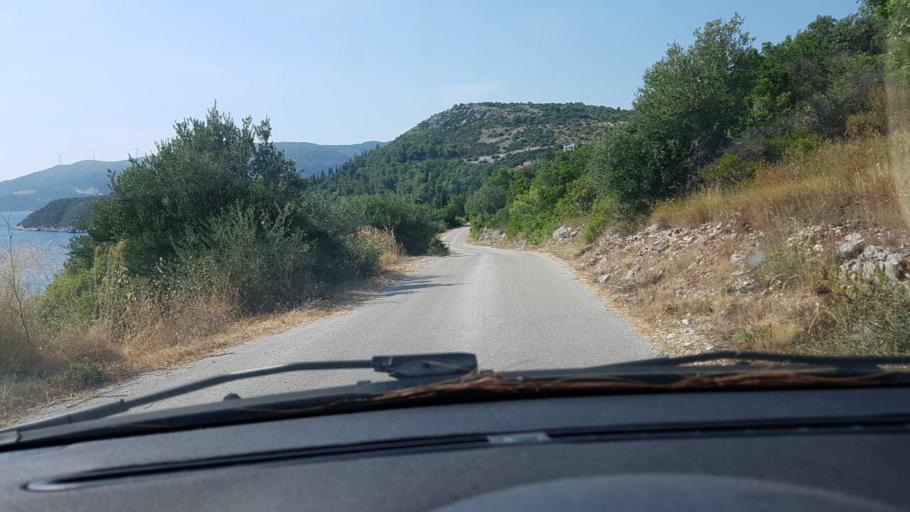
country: HR
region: Dubrovacko-Neretvanska
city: Podgora
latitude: 42.7804
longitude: 17.8625
